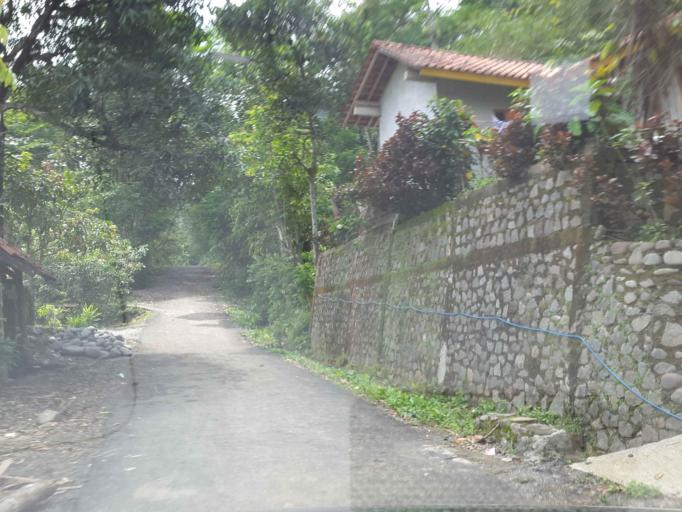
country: ID
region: Central Java
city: Jambuluwuk
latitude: -7.3238
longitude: 109.0041
